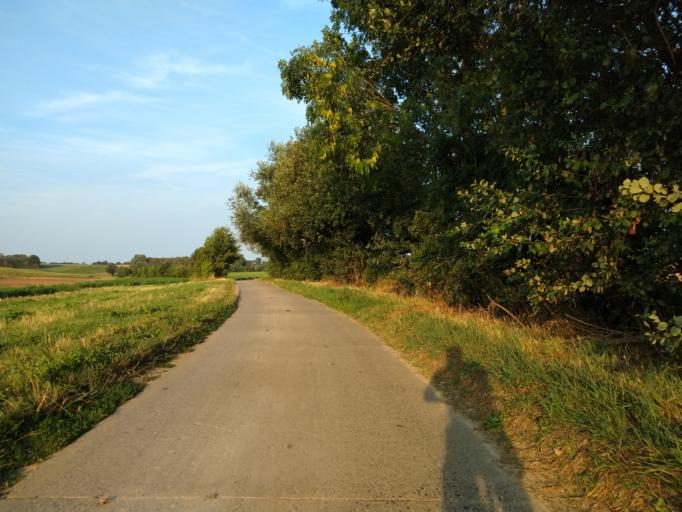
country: BE
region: Flanders
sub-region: Provincie Vlaams-Brabant
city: Hoegaarden
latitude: 50.7843
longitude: 4.8875
